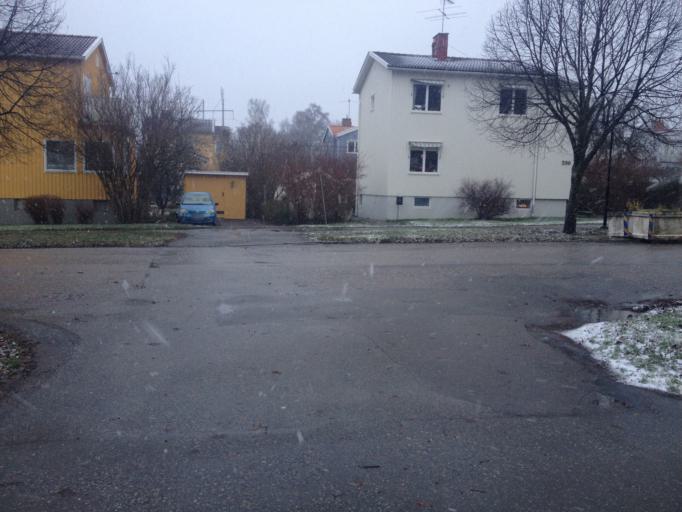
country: SE
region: Stockholm
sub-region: Stockholms Kommun
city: Bromma
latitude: 59.3532
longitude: 17.9006
